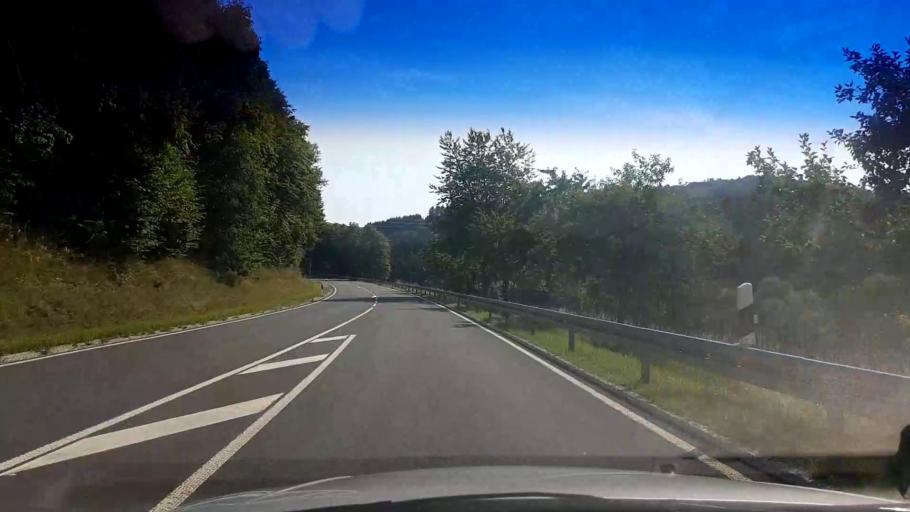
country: DE
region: Bavaria
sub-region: Upper Franconia
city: Plankenfels
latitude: 49.9340
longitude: 11.3888
